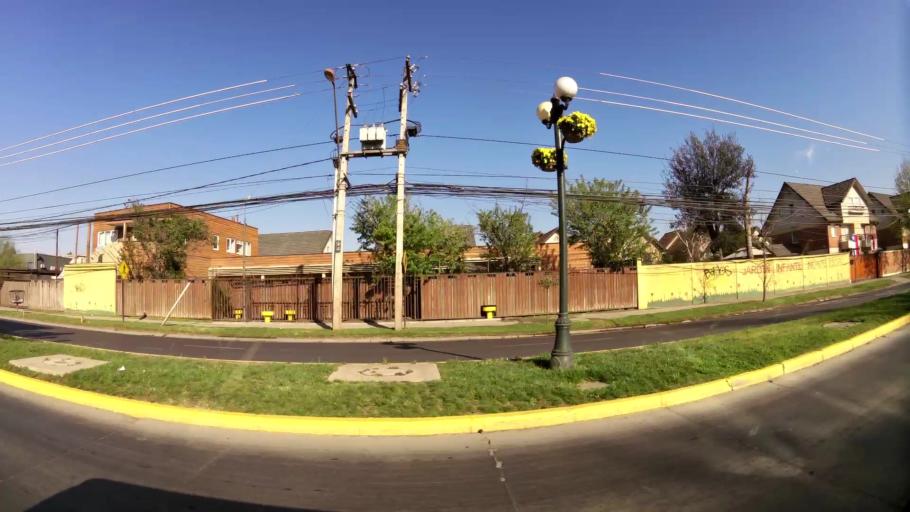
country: CL
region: Santiago Metropolitan
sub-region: Provincia de Chacabuco
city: Chicureo Abajo
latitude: -33.3640
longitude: -70.6704
